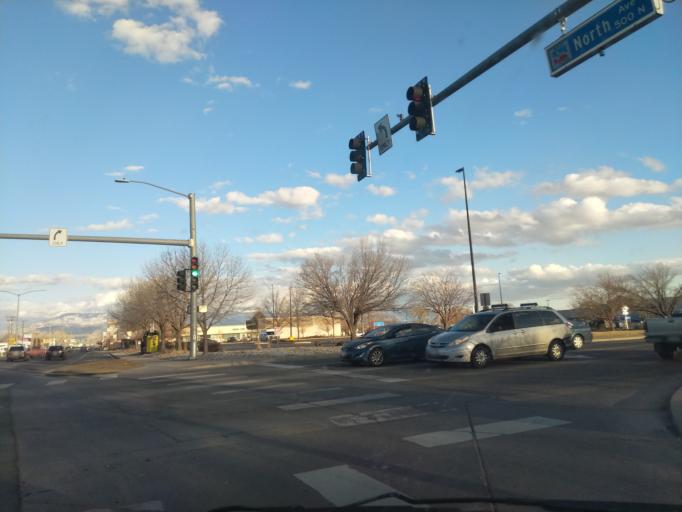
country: US
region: Colorado
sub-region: Mesa County
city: Fruitvale
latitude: 39.0773
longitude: -108.5201
